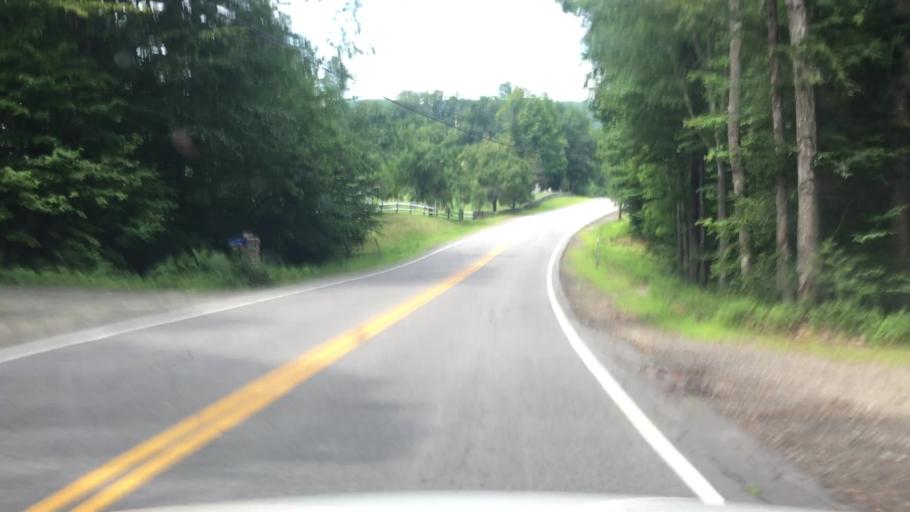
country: US
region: New Hampshire
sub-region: Grafton County
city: Rumney
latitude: 43.8012
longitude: -71.8025
